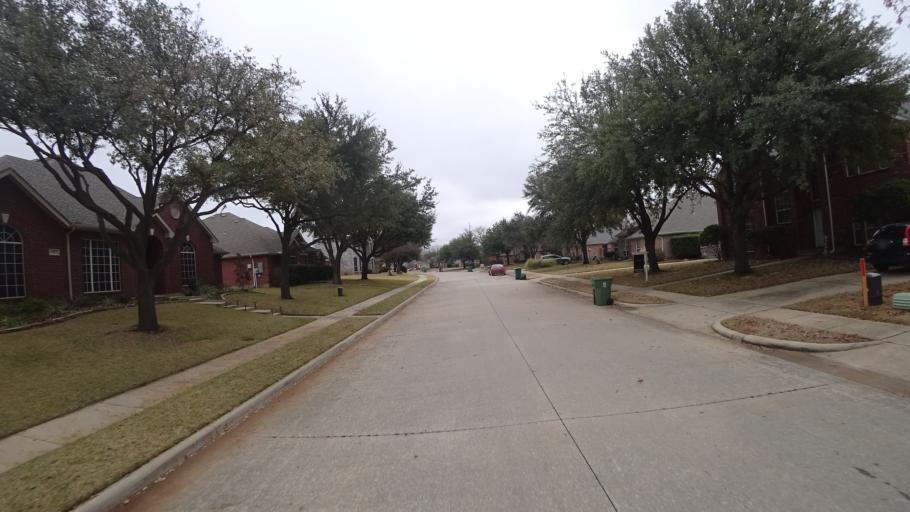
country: US
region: Texas
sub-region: Denton County
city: Lewisville
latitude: 33.0288
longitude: -97.0333
